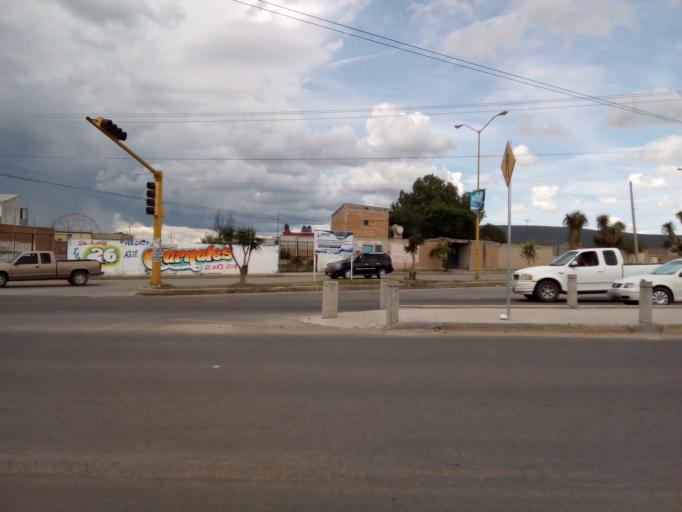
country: MX
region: Guerrero
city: San Luis de la Paz
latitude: 21.2882
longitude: -100.5221
